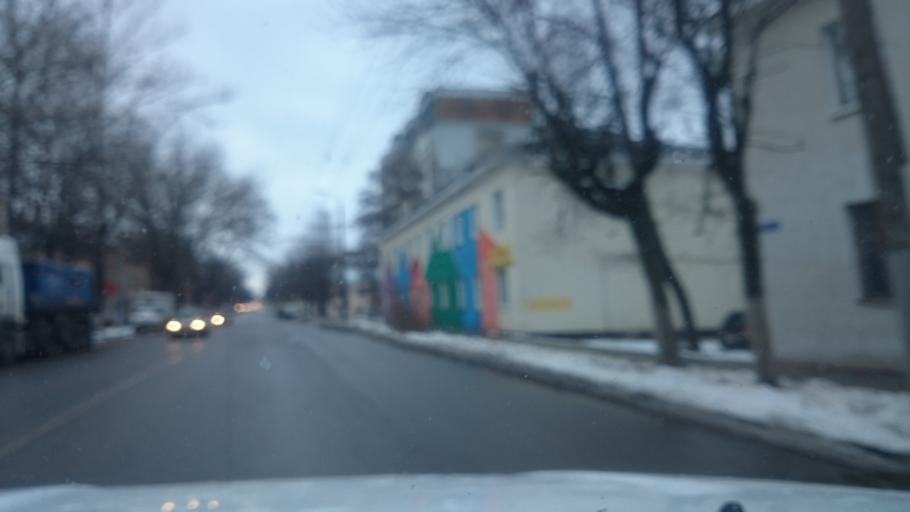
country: RU
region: Tula
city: Mendeleyevskiy
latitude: 54.1678
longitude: 37.5765
